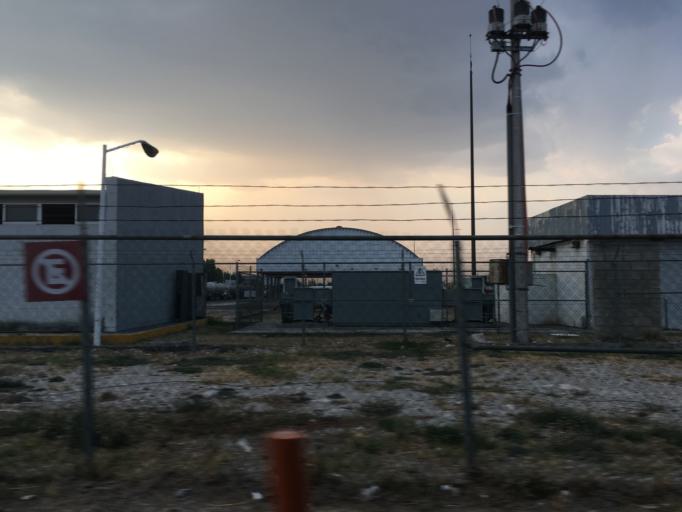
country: MX
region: Jalisco
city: El Quince
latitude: 20.5290
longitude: -103.2981
